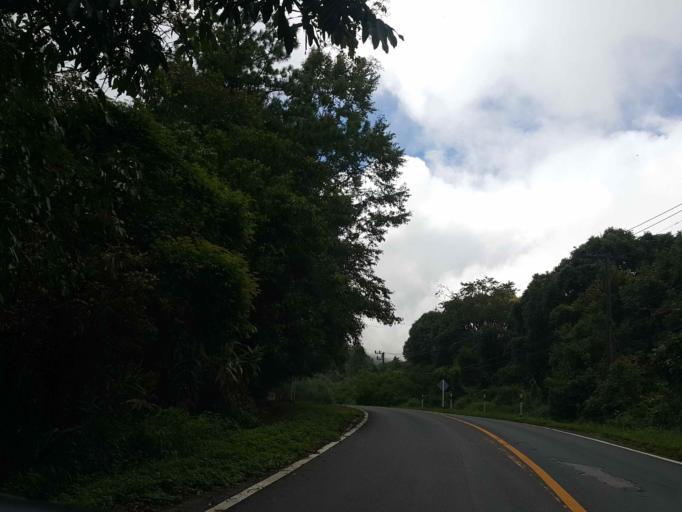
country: TH
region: Chiang Mai
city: Mae Chaem
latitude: 18.5382
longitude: 98.4906
